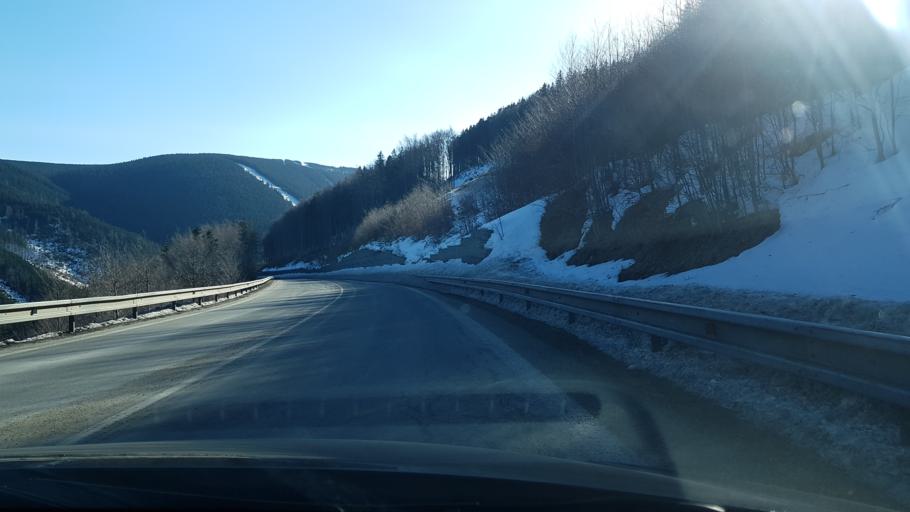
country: CZ
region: Olomoucky
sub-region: Okres Jesenik
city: Jesenik
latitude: 50.1438
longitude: 17.1623
